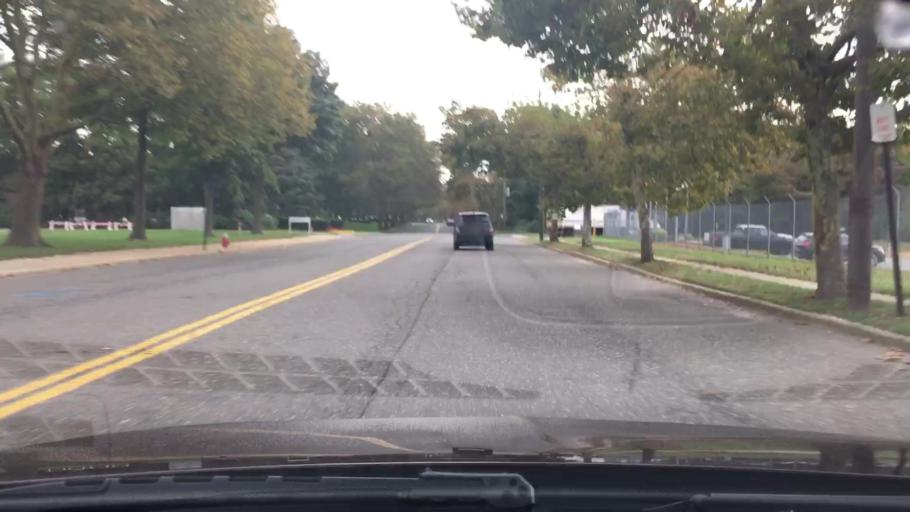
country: US
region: New York
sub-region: Suffolk County
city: Melville
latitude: 40.7670
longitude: -73.4199
